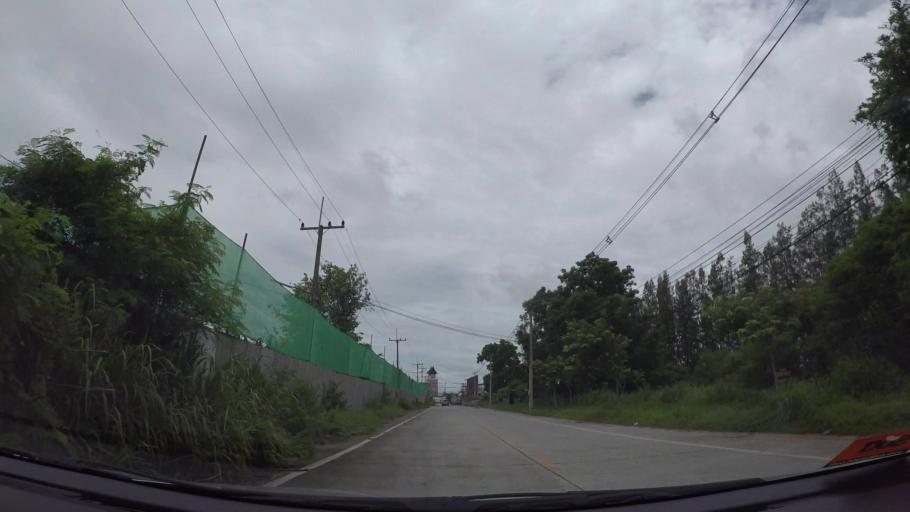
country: TH
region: Chon Buri
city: Si Racha
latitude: 13.1563
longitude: 100.9838
